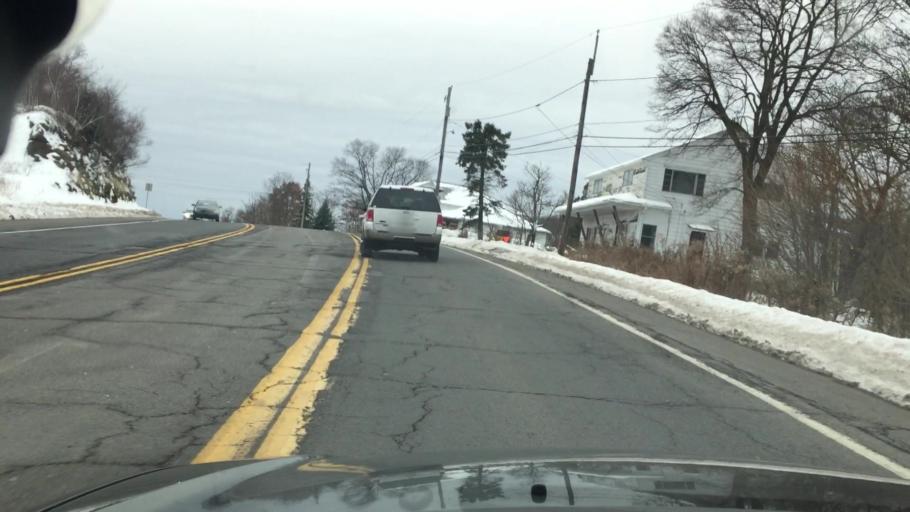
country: US
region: Pennsylvania
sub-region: Luzerne County
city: Mountain Top
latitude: 41.1773
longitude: -75.8821
